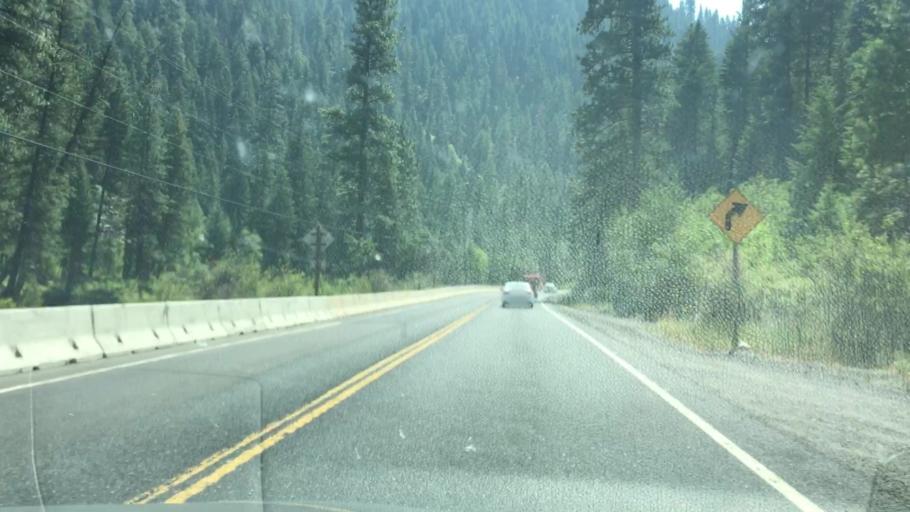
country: US
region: Idaho
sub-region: Valley County
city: McCall
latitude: 45.1322
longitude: -116.2848
